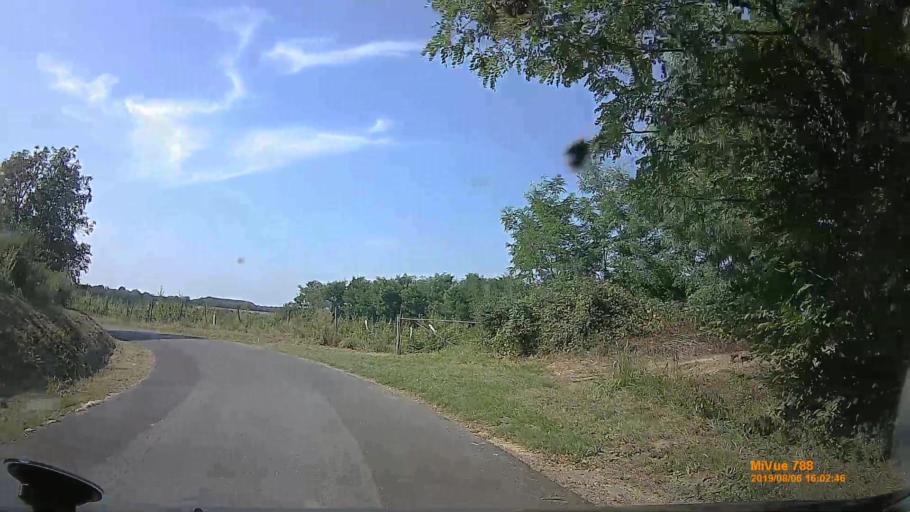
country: HU
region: Zala
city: Murakeresztur
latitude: 46.3045
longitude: 16.9732
